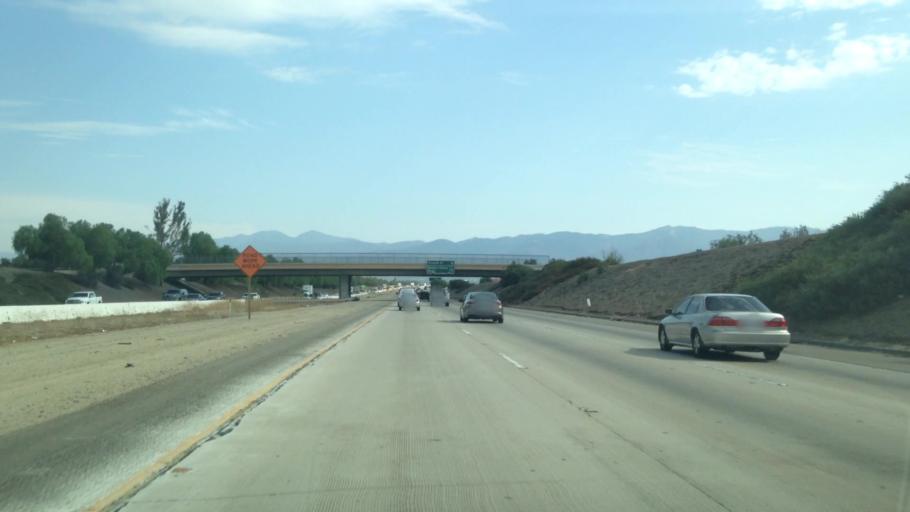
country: US
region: California
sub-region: Riverside County
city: Norco
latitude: 33.9261
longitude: -117.5566
